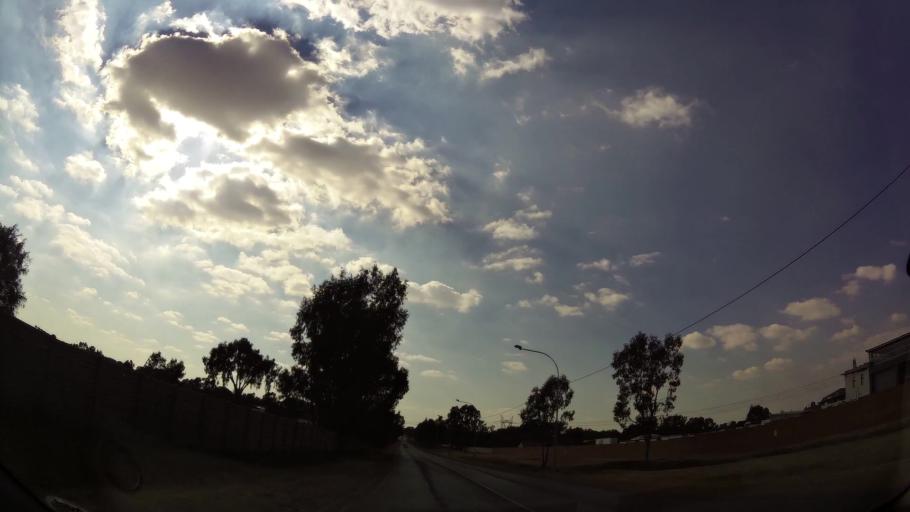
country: ZA
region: Gauteng
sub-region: Ekurhuleni Metropolitan Municipality
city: Benoni
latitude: -26.1019
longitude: 28.3535
